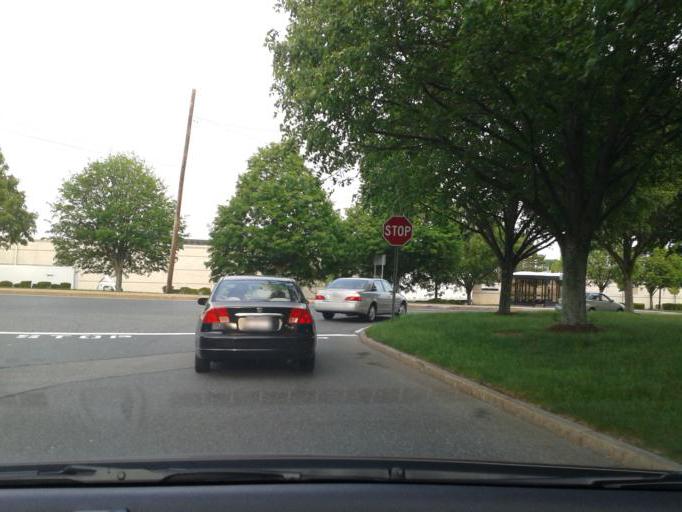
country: US
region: Massachusetts
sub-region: Middlesex County
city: Framingham
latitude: 42.3037
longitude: -71.3980
